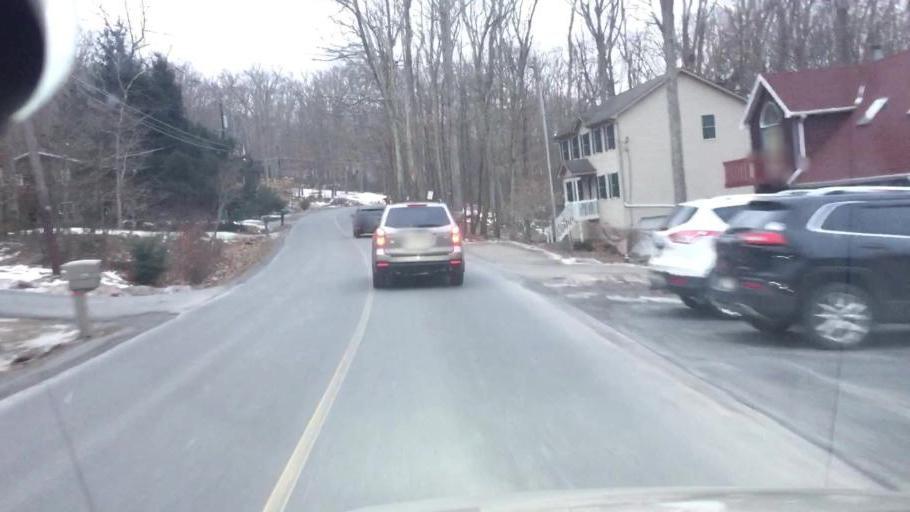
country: US
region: Pennsylvania
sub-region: Luzerne County
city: Oakdale
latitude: 41.0327
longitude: -75.9494
